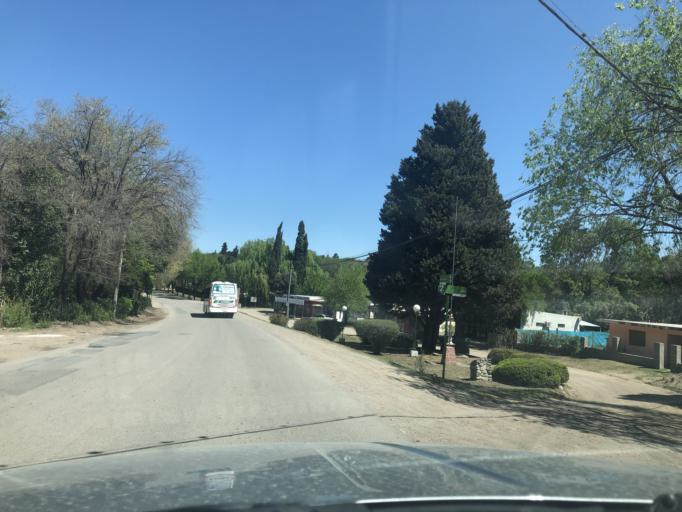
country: AR
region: Cordoba
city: La Granja
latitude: -31.0184
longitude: -64.2737
